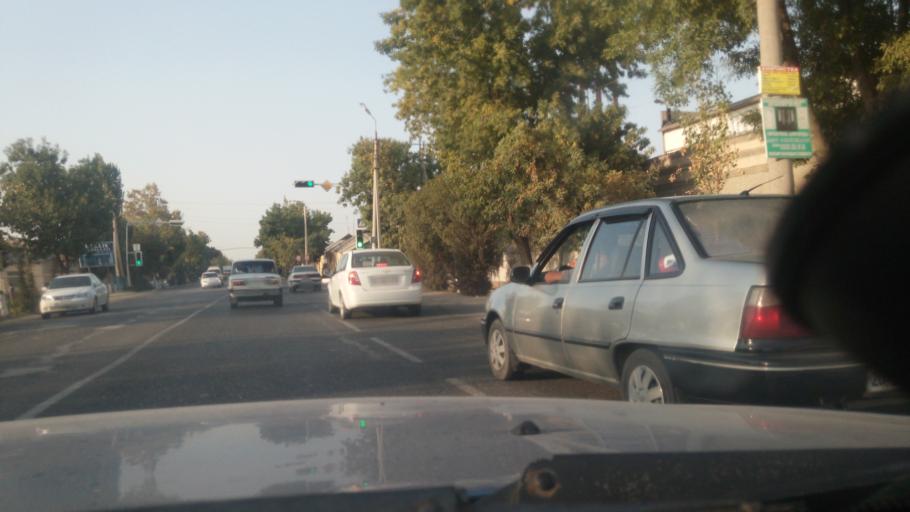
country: UZ
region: Sirdaryo
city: Guliston
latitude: 40.4775
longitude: 68.7764
